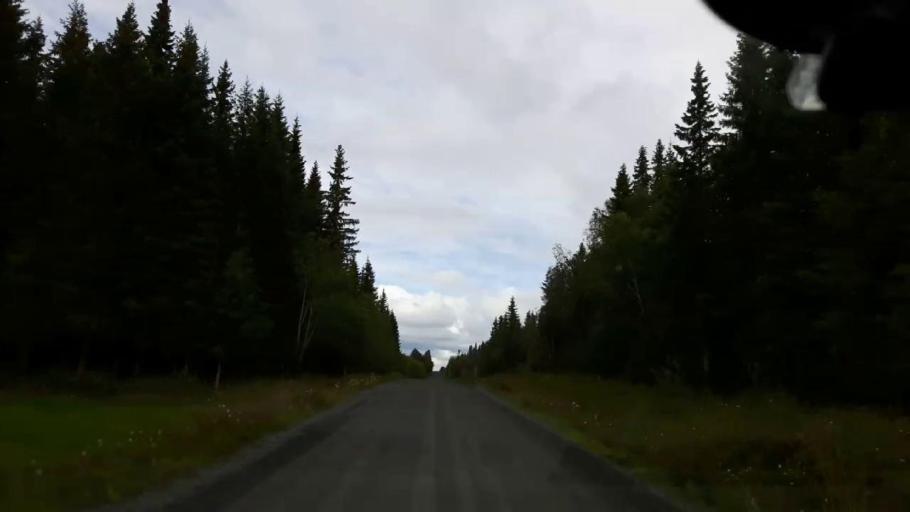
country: SE
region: Jaemtland
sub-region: Krokoms Kommun
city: Valla
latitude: 63.5050
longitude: 13.9587
